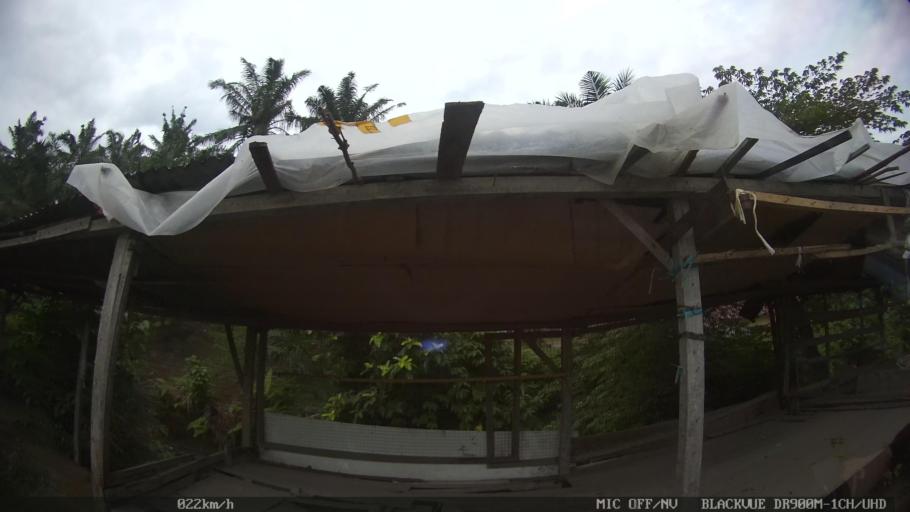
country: ID
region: North Sumatra
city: Sunggal
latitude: 3.5910
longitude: 98.5667
